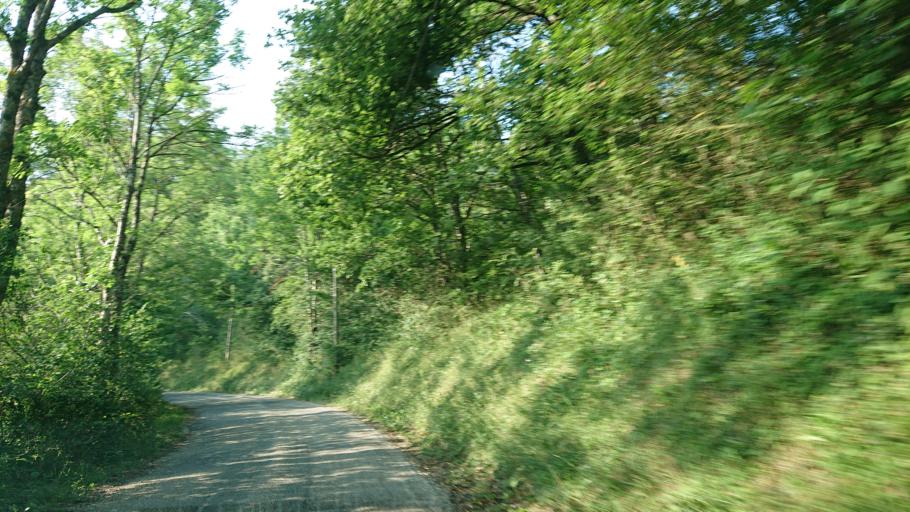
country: FR
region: Rhone-Alpes
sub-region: Departement de l'Isere
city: La Mure
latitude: 44.8171
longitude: 5.9364
